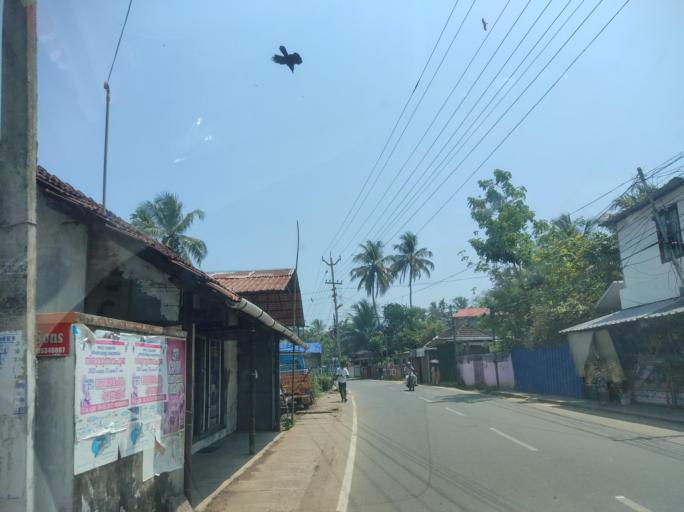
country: IN
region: Kerala
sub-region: Ernakulam
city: Cochin
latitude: 9.8927
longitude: 76.2848
